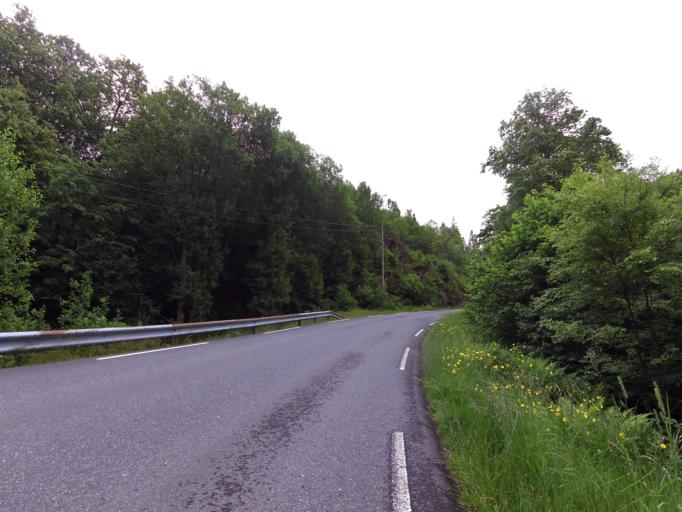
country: NO
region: Vest-Agder
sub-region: Lyngdal
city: Lyngdal
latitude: 58.1041
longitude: 6.9624
